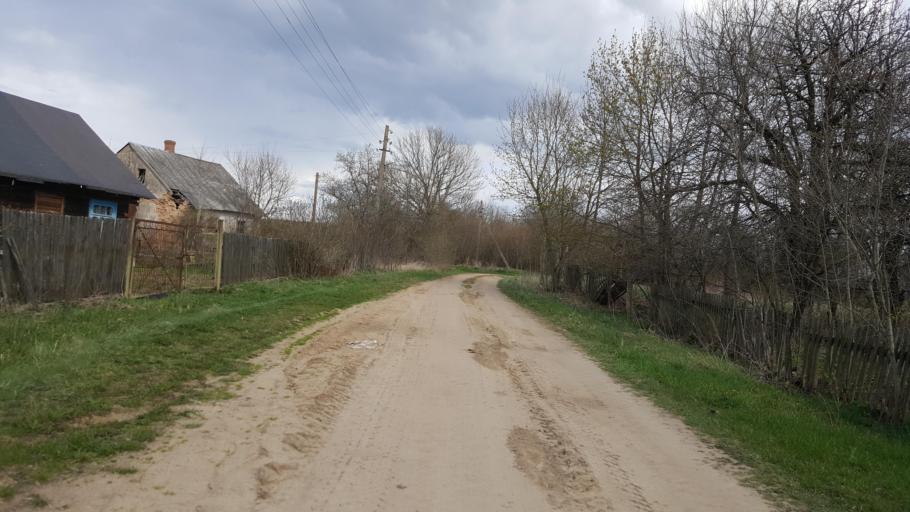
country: BY
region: Brest
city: Kamyanyets
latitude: 52.4427
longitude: 23.6701
